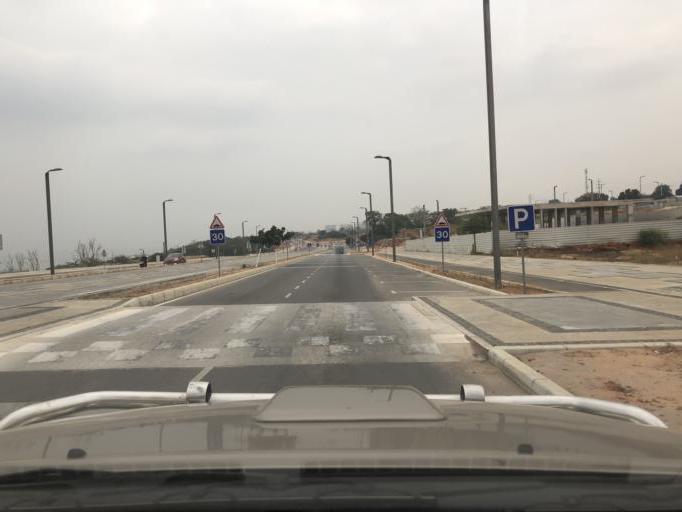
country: AO
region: Luanda
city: Luanda
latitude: -8.9025
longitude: 13.1740
